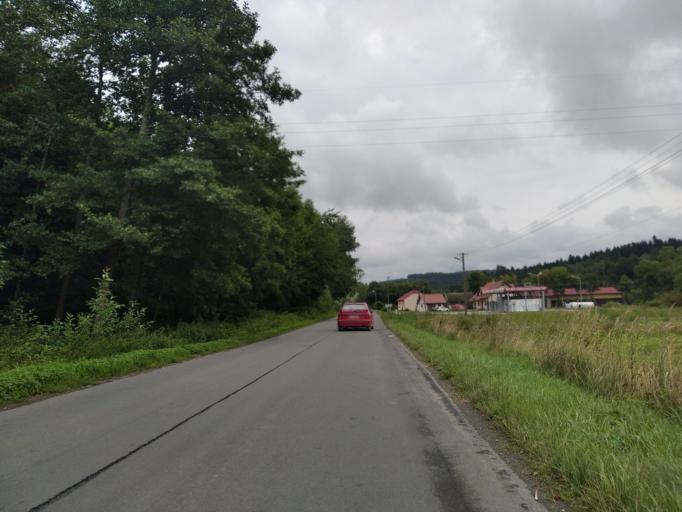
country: PL
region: Subcarpathian Voivodeship
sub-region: Powiat przemyski
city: Bircza
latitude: 49.6907
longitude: 22.4374
